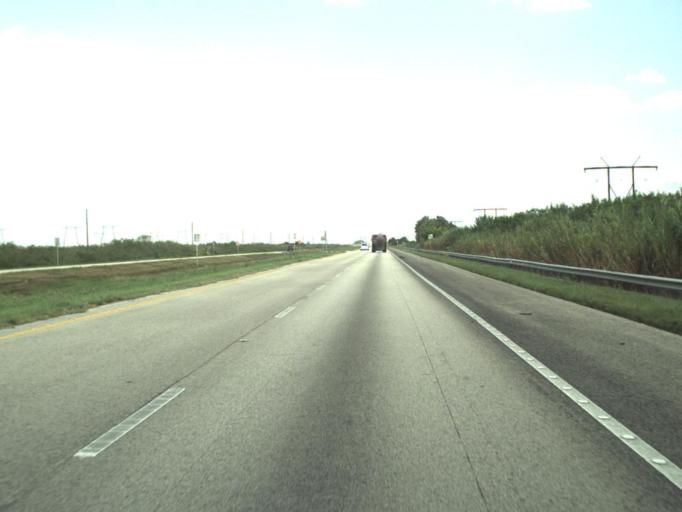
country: US
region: Florida
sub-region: Broward County
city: Weston
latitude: 26.3078
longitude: -80.5168
